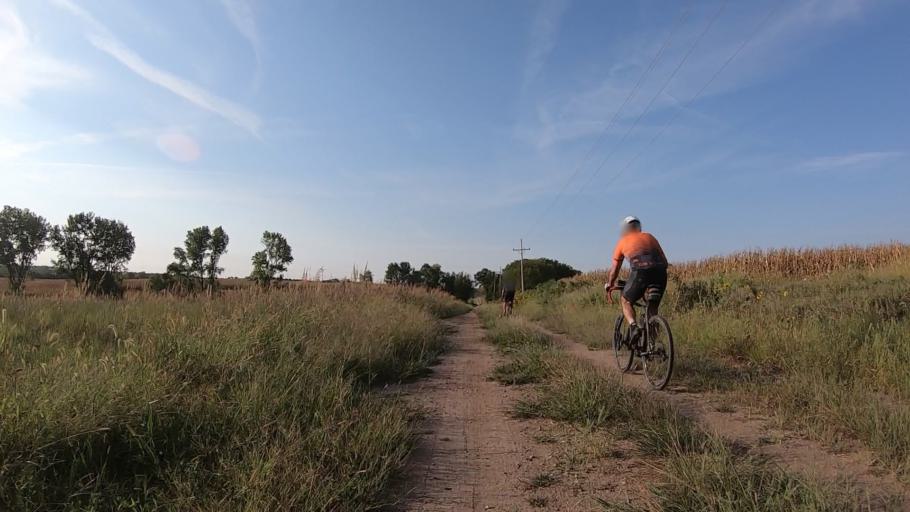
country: US
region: Kansas
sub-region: Marshall County
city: Blue Rapids
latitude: 39.7063
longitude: -96.7792
